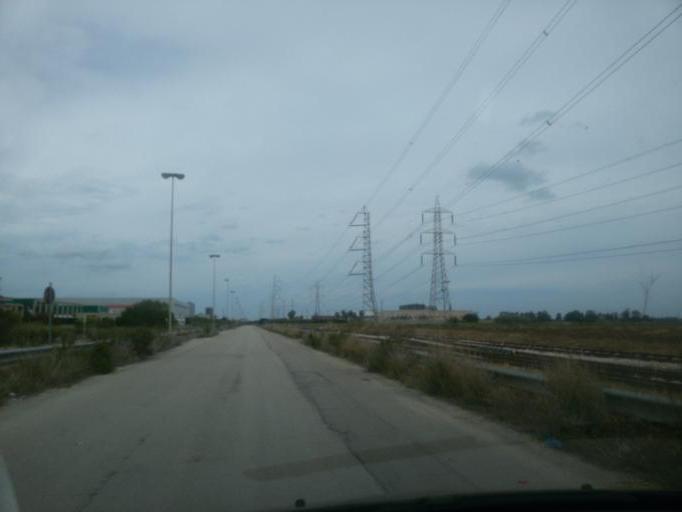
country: IT
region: Apulia
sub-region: Provincia di Brindisi
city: Materdomini
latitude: 40.6280
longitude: 17.9816
